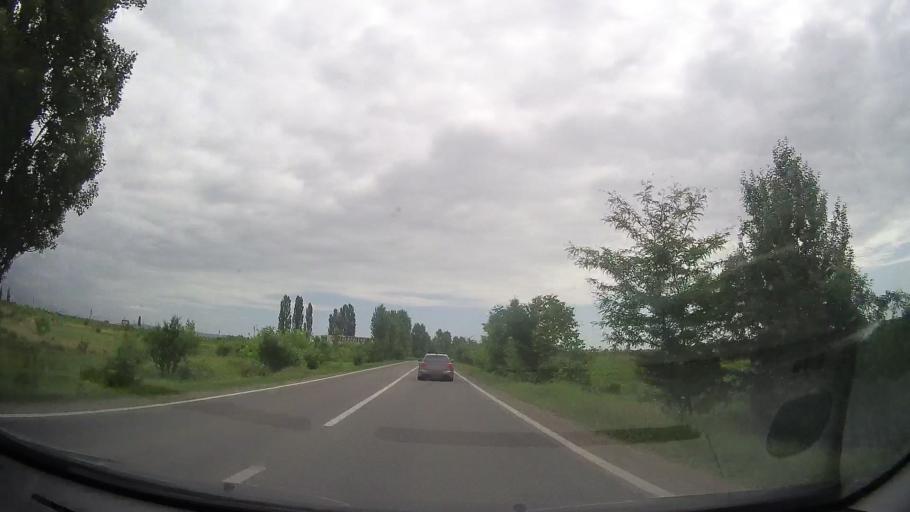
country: RO
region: Prahova
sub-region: Comuna Barcanesti
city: Barcanesti
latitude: 44.8924
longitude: 26.0502
